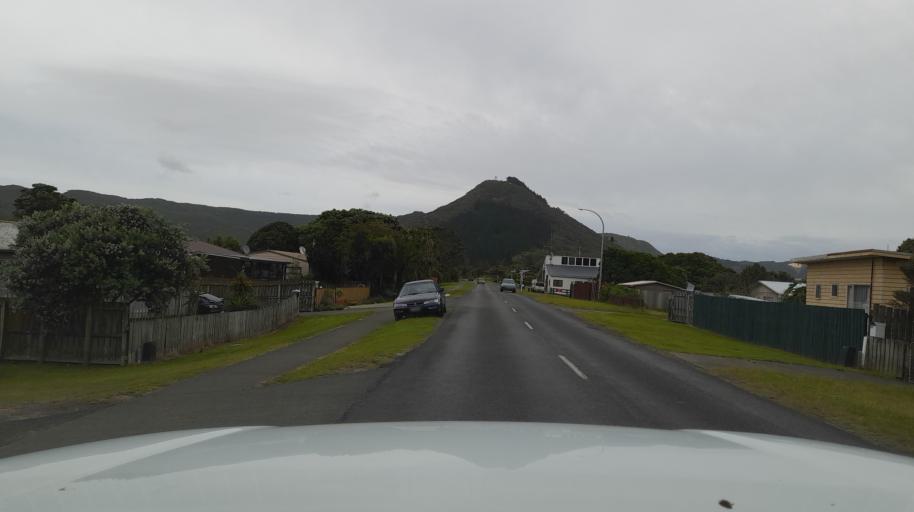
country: NZ
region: Northland
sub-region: Far North District
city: Ahipara
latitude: -35.1657
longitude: 173.1558
